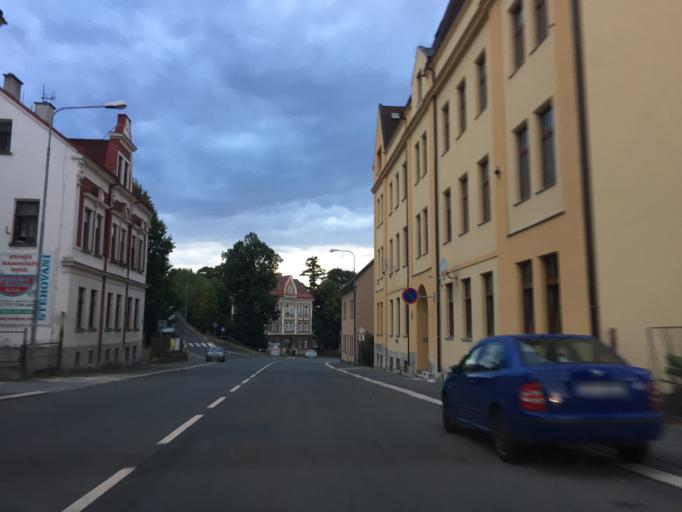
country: CZ
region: Liberecky
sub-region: Okres Jablonec nad Nisou
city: Jablonec nad Nisou
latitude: 50.7156
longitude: 15.1664
